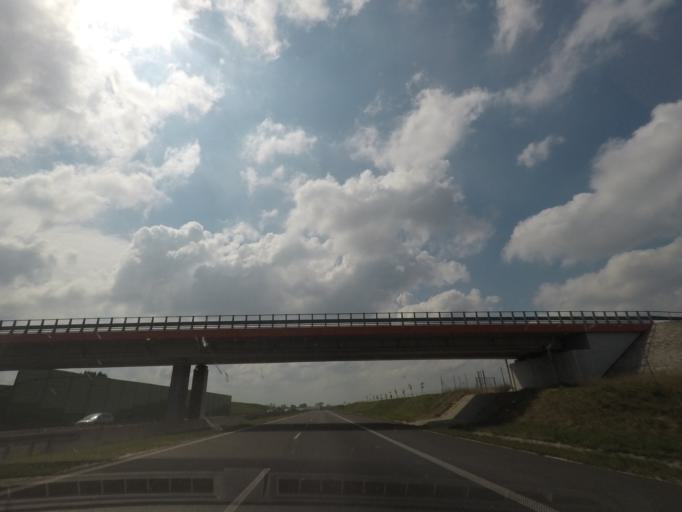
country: PL
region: Lodz Voivodeship
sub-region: Powiat kutnowski
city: Krzyzanow
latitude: 52.1570
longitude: 19.4824
